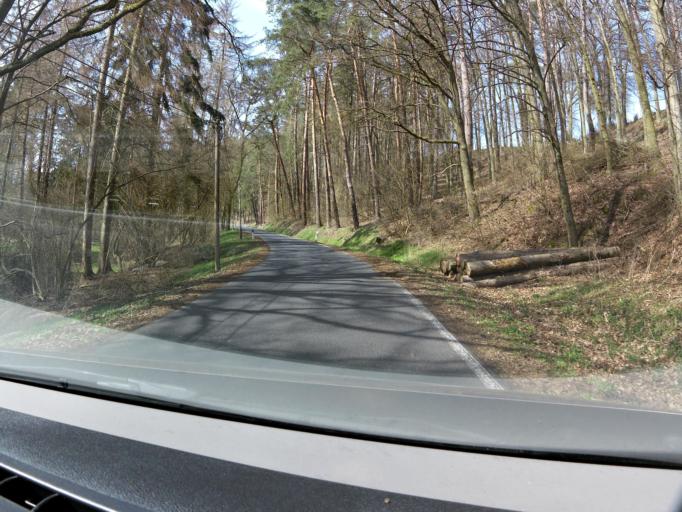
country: DE
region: Thuringia
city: Frauensee
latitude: 50.8660
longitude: 10.1369
